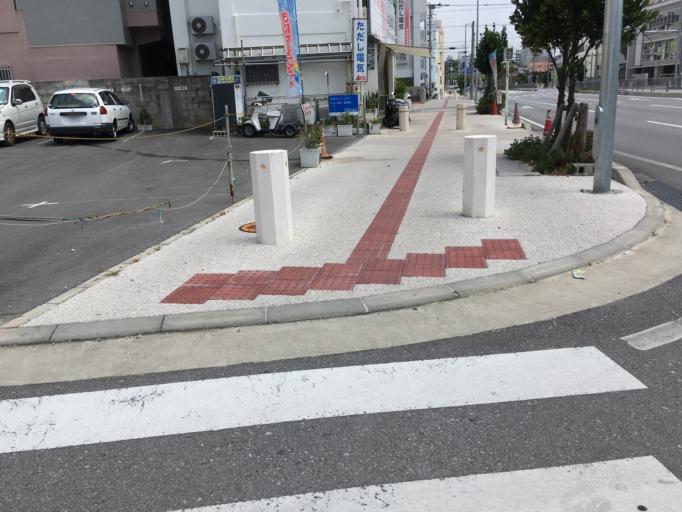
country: JP
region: Okinawa
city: Naha-shi
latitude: 26.2212
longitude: 127.6744
